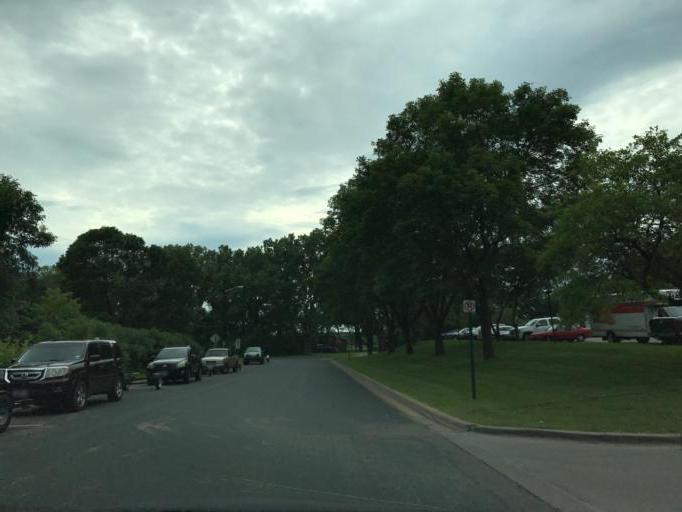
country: US
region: Minnesota
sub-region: Hennepin County
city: Osseo
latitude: 45.0801
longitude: -93.4043
